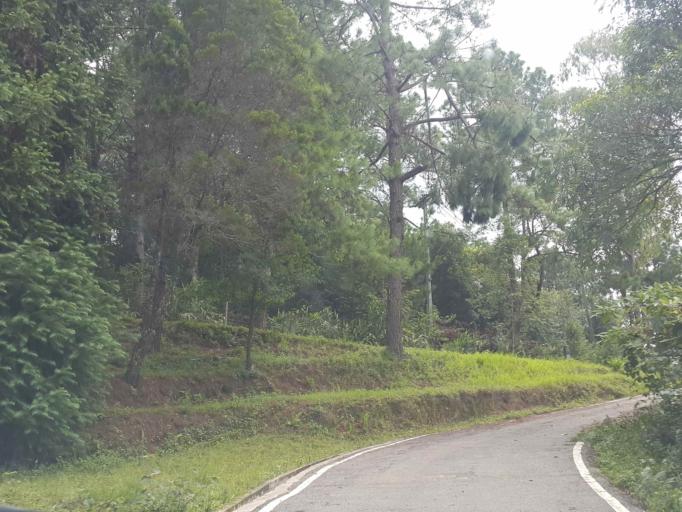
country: TH
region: Chiang Mai
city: Mae Chaem
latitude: 18.5187
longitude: 98.5324
